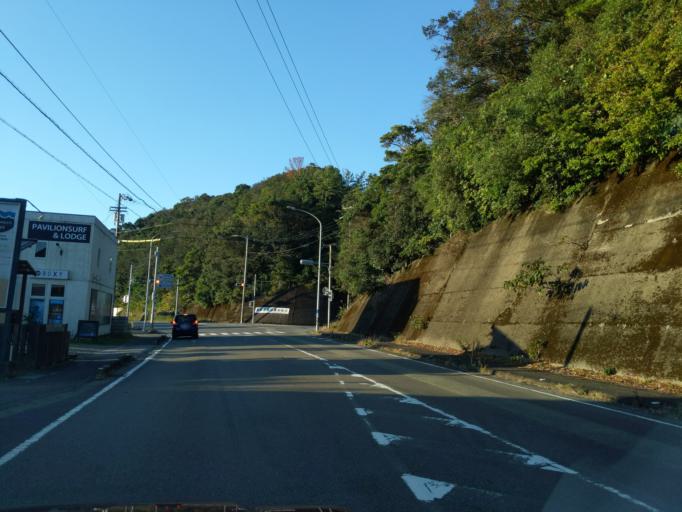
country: JP
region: Kochi
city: Muroto-misakicho
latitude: 33.5723
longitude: 134.3084
